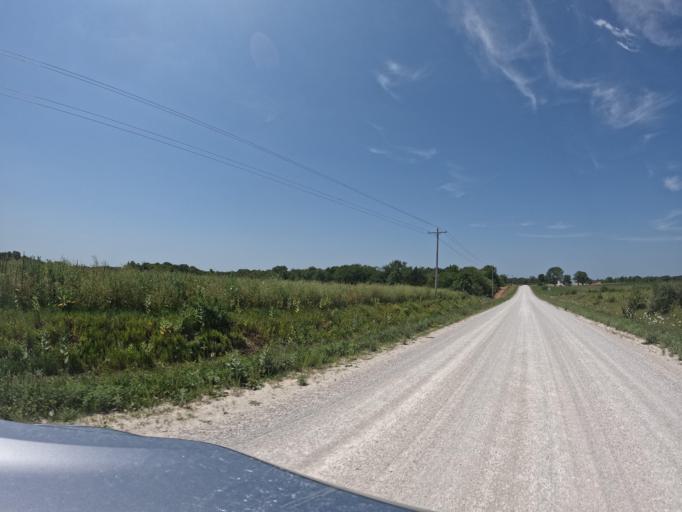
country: US
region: Iowa
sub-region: Henry County
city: Mount Pleasant
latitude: 40.9048
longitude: -91.5403
